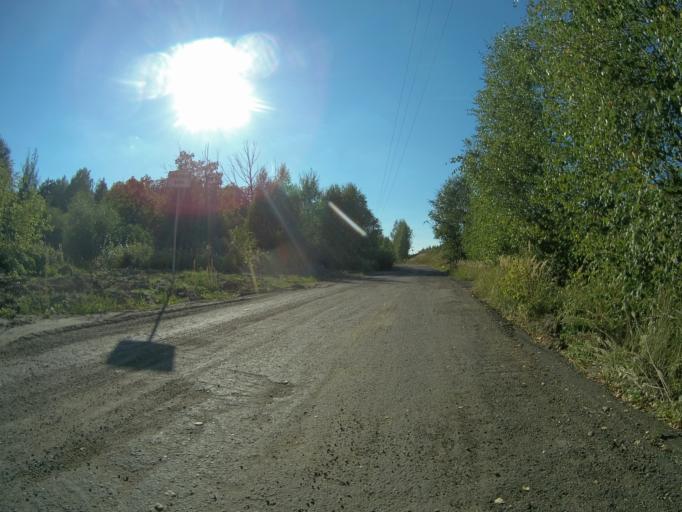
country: RU
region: Vladimir
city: Kommunar
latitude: 56.0531
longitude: 40.4182
